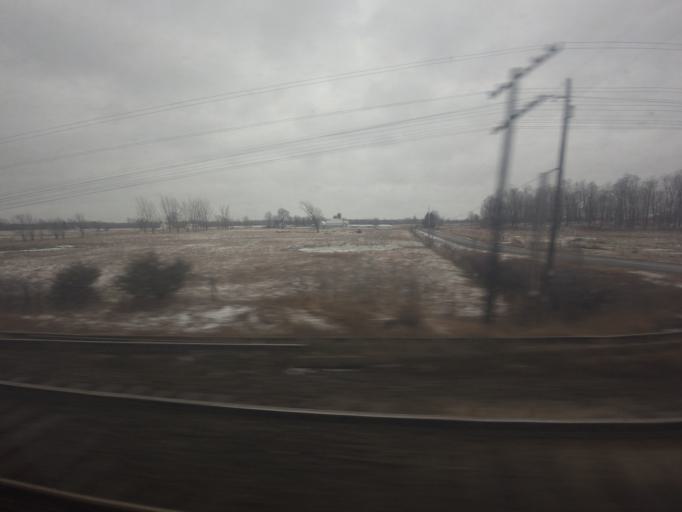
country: CA
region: Ontario
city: Gananoque
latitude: 44.3541
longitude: -76.2360
